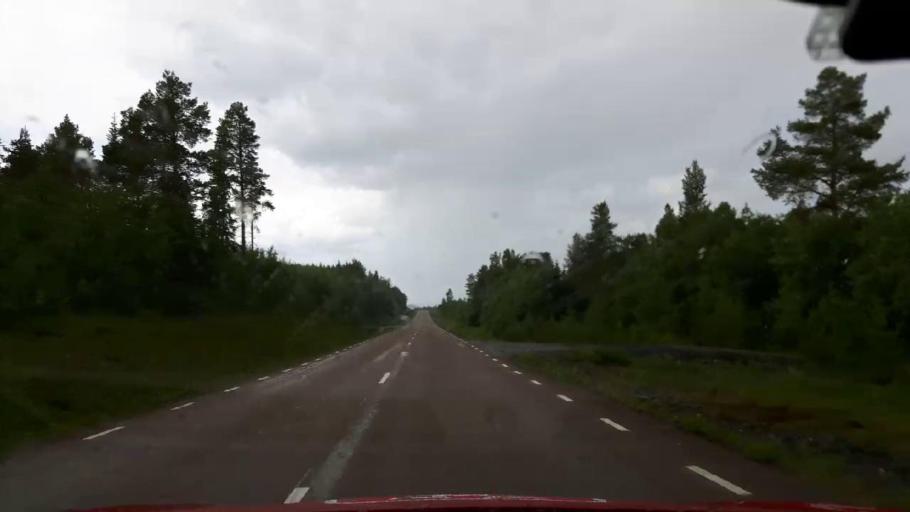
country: SE
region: Jaemtland
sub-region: Krokoms Kommun
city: Krokom
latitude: 63.8837
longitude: 14.2855
